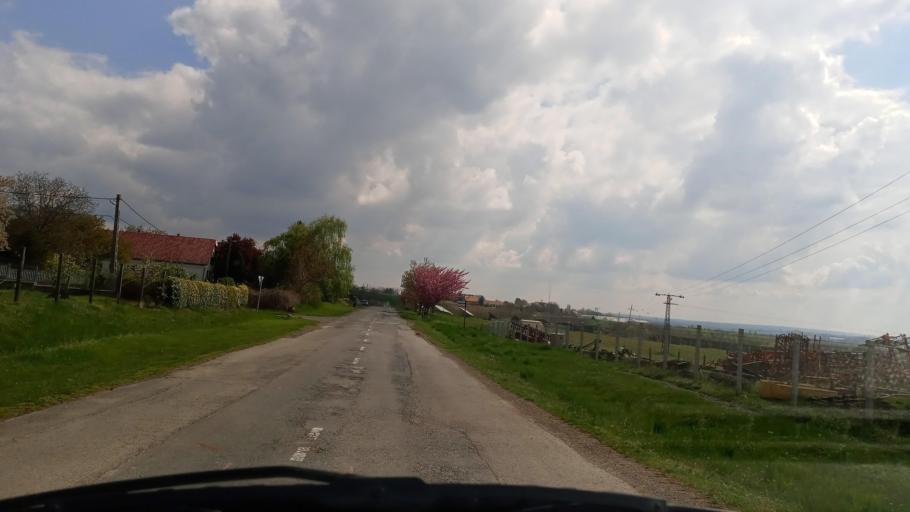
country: HU
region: Baranya
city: Pecsvarad
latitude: 46.1068
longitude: 18.5214
